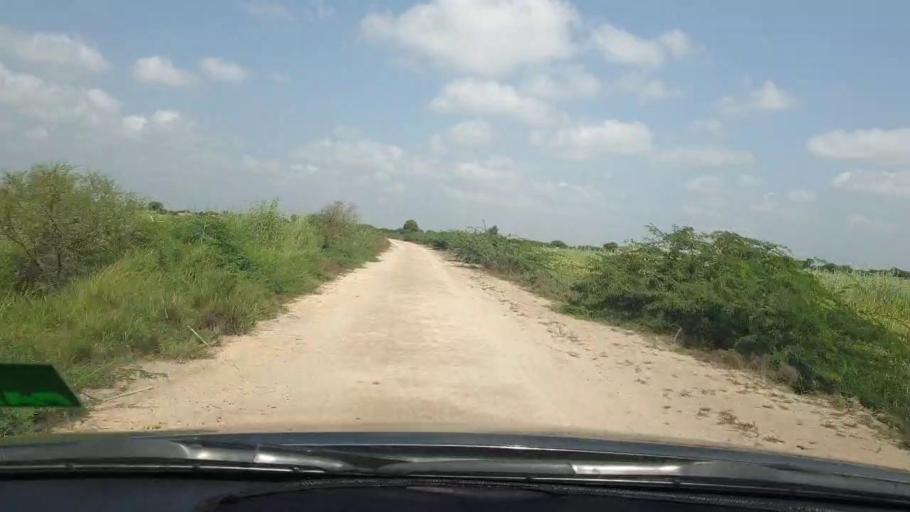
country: PK
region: Sindh
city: Tando Bago
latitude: 24.8704
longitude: 69.0355
